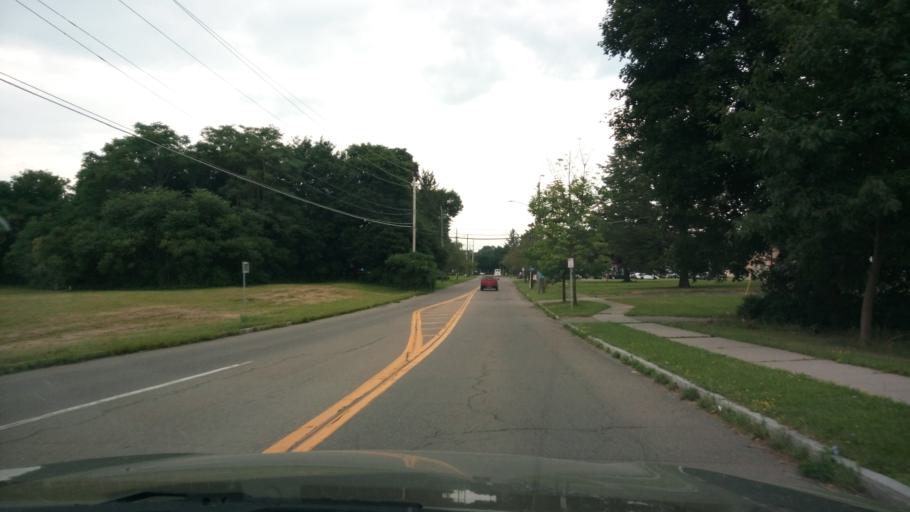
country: US
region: New York
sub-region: Chemung County
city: Elmira Heights
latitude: 42.1168
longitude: -76.8085
